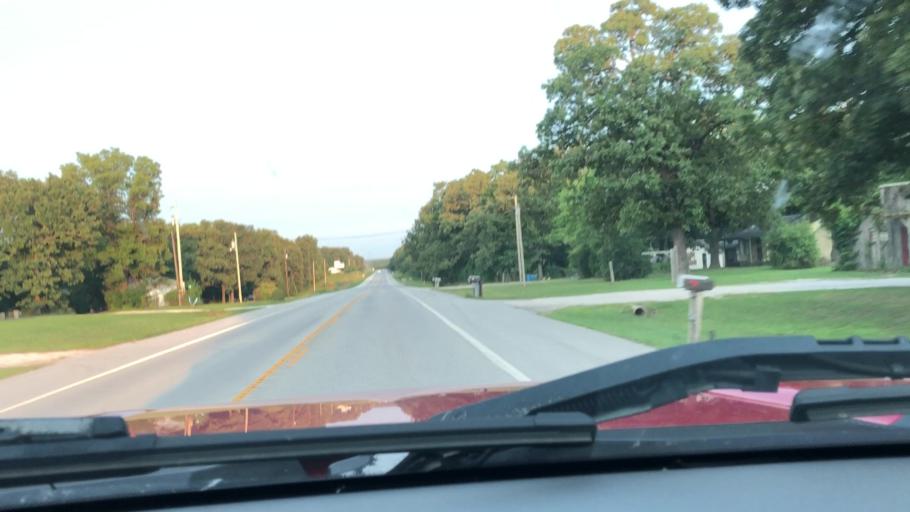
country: US
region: Missouri
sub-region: Jasper County
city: Duquesne
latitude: 36.9753
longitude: -94.4593
